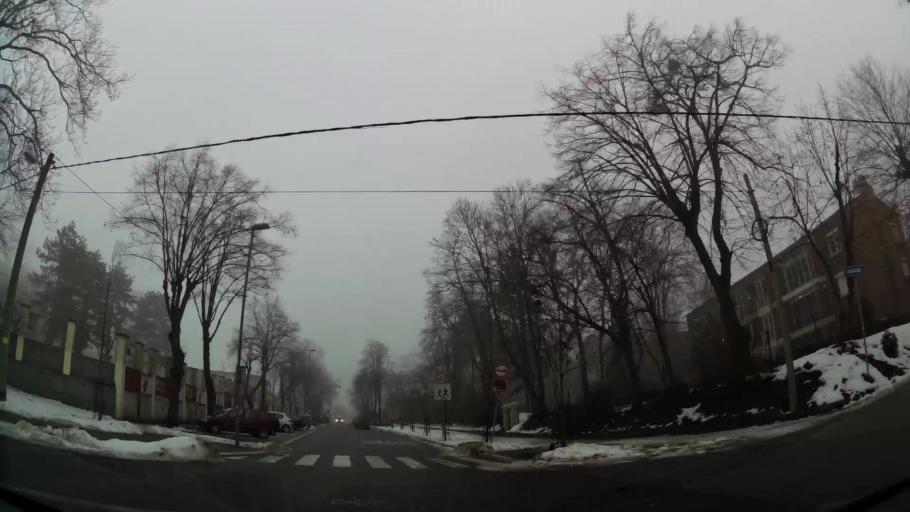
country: RS
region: Central Serbia
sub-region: Belgrade
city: Savski Venac
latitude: 44.7900
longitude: 20.4406
